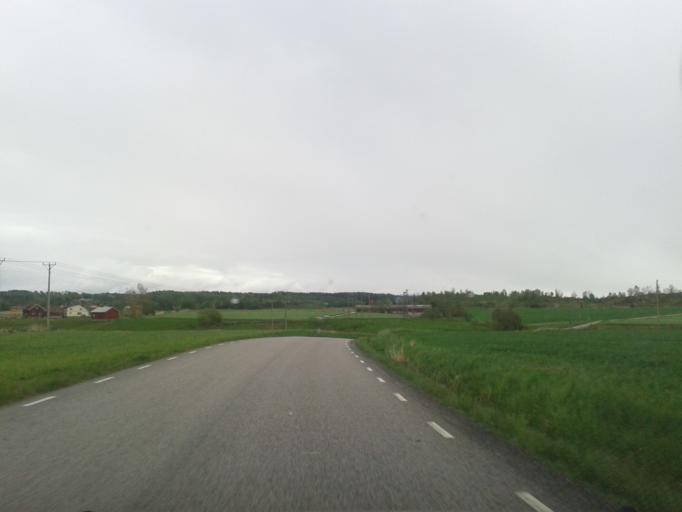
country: SE
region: Vaestra Goetaland
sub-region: Kungalvs Kommun
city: Kode
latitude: 57.9366
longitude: 11.8236
